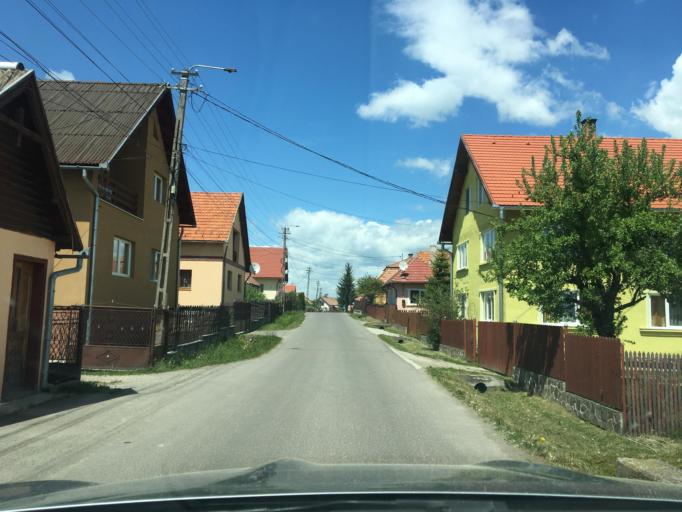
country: RO
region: Harghita
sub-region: Comuna Remetea
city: Remetea
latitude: 46.8023
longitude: 25.4532
